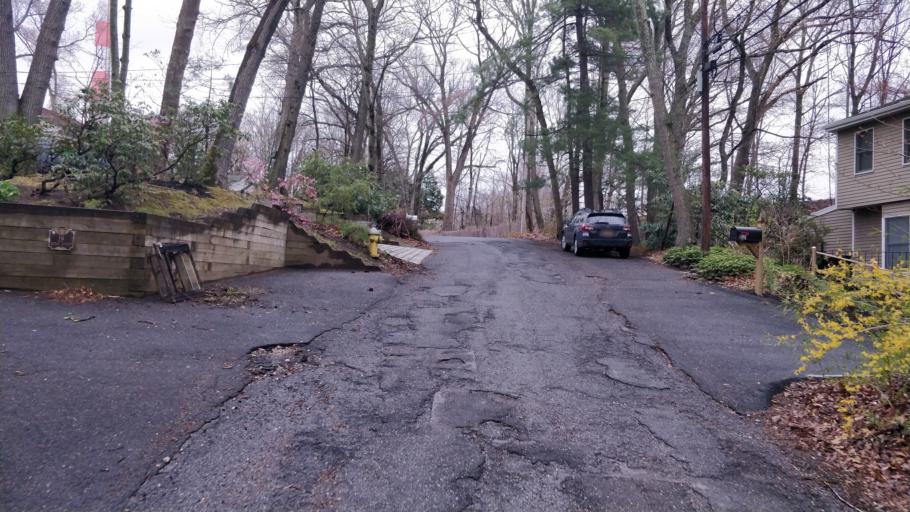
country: US
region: New York
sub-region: Suffolk County
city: Port Jefferson
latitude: 40.9503
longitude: -73.0825
